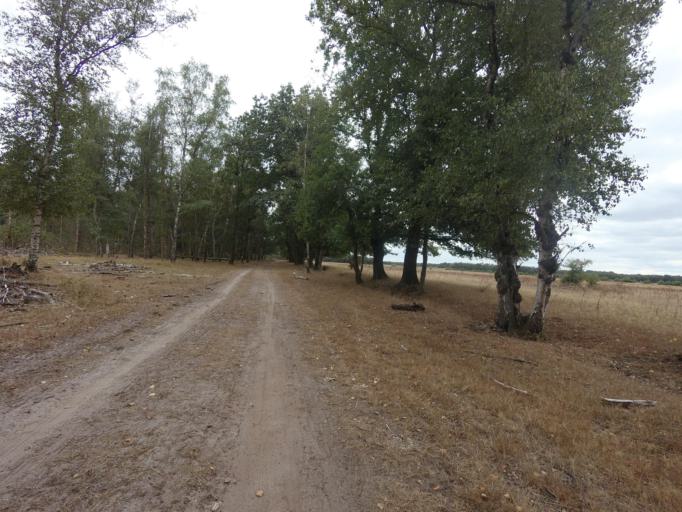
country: NL
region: North Brabant
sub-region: Gemeente Landerd
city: Schaijk
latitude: 51.7091
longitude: 5.6183
